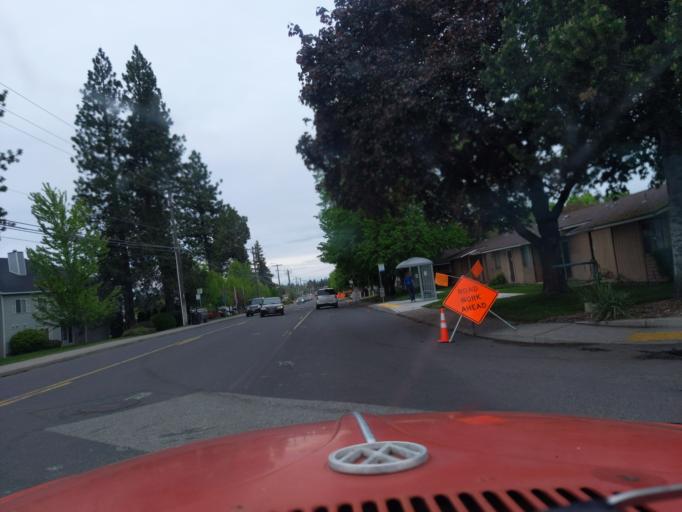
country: US
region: Washington
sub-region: Spokane County
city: Spokane
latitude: 47.6059
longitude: -117.3683
